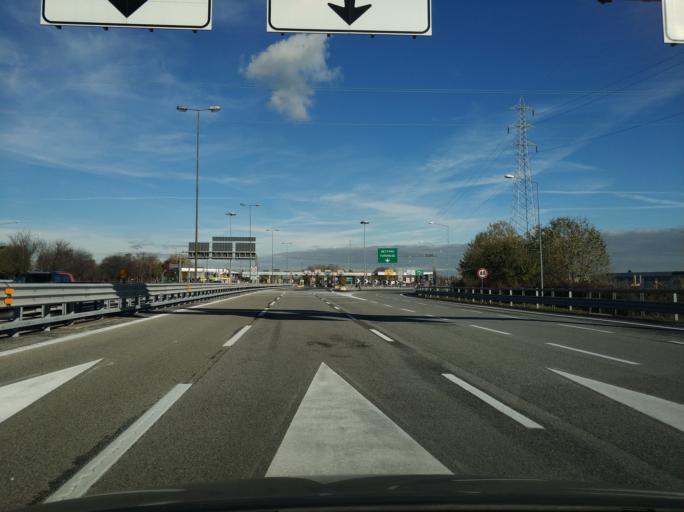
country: IT
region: Piedmont
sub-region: Provincia di Torino
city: Settimo Torinese
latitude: 45.1438
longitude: 7.7334
